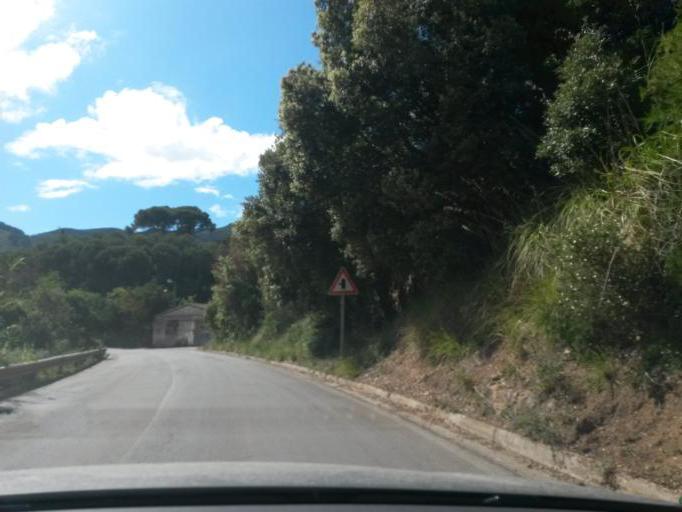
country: IT
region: Tuscany
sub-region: Provincia di Livorno
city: Rio Marina
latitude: 42.8138
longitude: 10.4182
